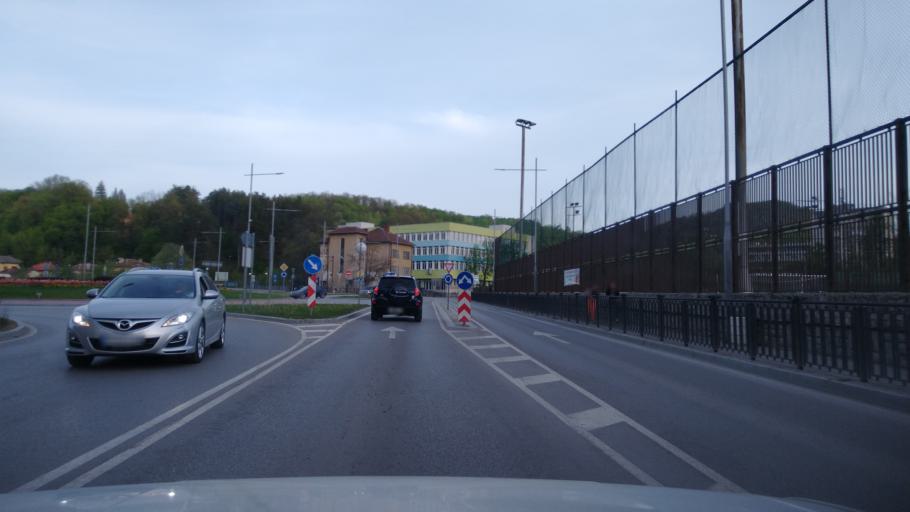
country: BG
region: Gabrovo
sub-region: Obshtina Gabrovo
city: Gabrovo
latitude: 42.8610
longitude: 25.3214
